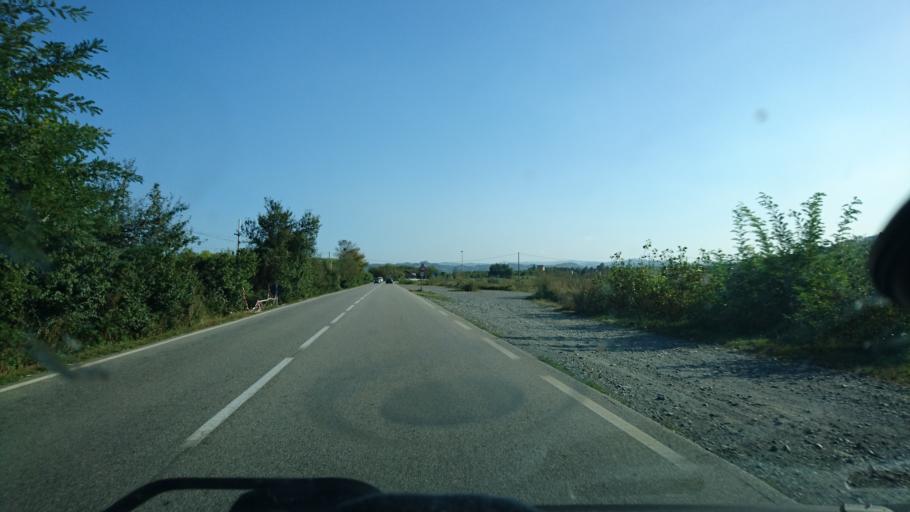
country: IT
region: Piedmont
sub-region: Provincia di Alessandria
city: Strevi
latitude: 44.7209
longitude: 8.5293
